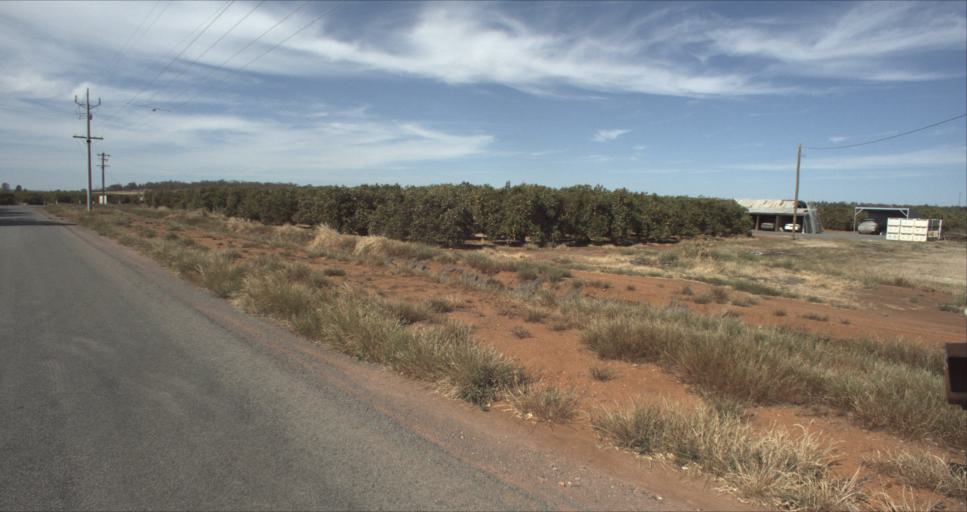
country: AU
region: New South Wales
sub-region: Leeton
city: Leeton
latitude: -34.5870
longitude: 146.4726
